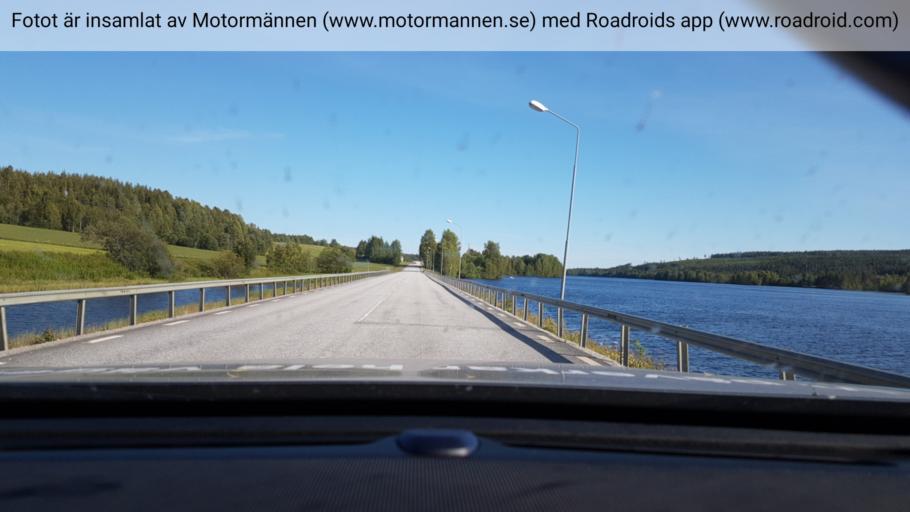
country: SE
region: Vaesterbotten
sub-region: Vindelns Kommun
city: Vindeln
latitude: 64.1765
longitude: 19.4812
